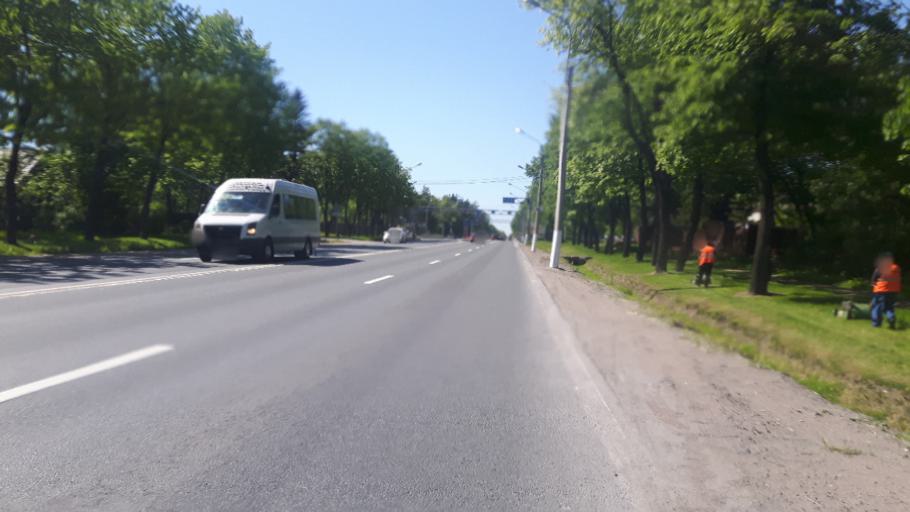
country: RU
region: Leningrad
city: Ol'gino
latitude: 59.8743
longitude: 29.9497
